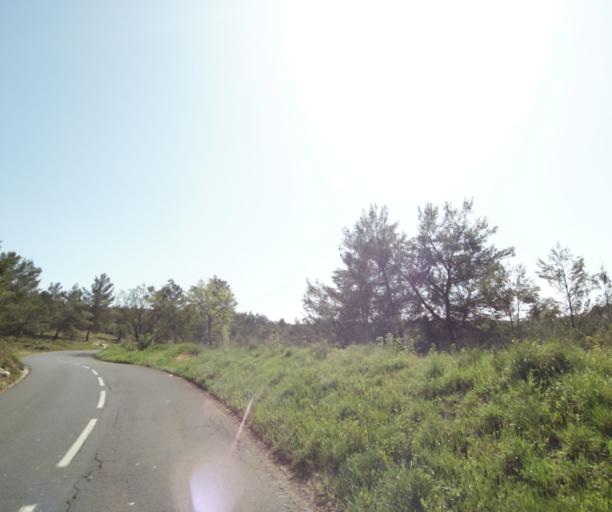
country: FR
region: Languedoc-Roussillon
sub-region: Departement de l'Herault
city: Grabels
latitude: 43.6488
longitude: 3.7773
